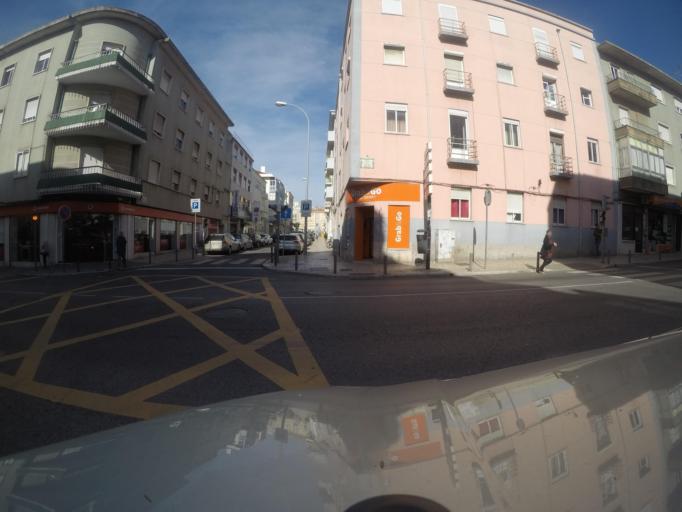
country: PT
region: Lisbon
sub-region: Amadora
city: Amadora
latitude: 38.7599
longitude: -9.2393
